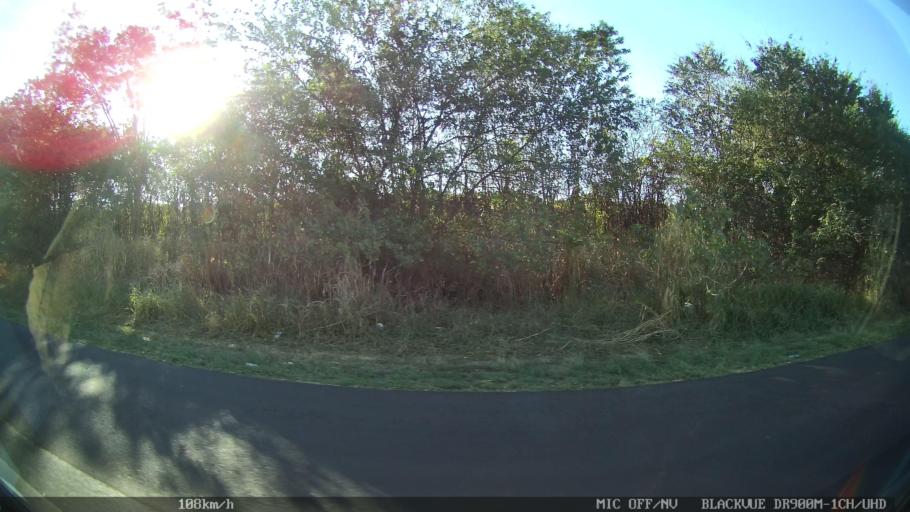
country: BR
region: Sao Paulo
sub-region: Guapiacu
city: Guapiacu
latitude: -20.7486
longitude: -49.1278
